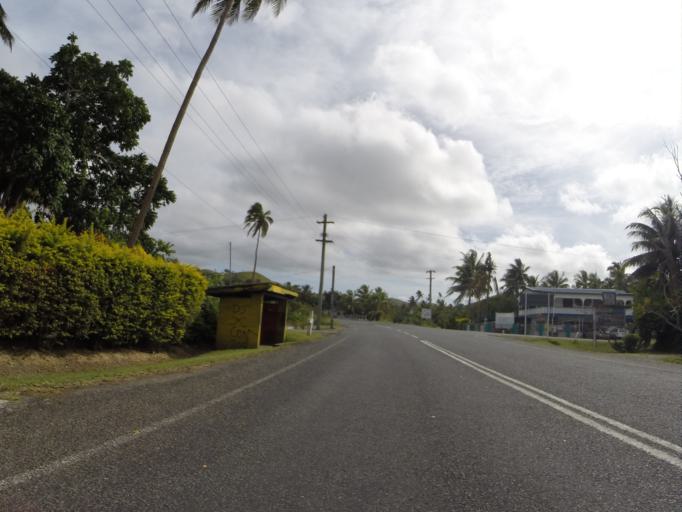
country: FJ
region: Western
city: Nadi
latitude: -18.1718
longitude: 177.5417
